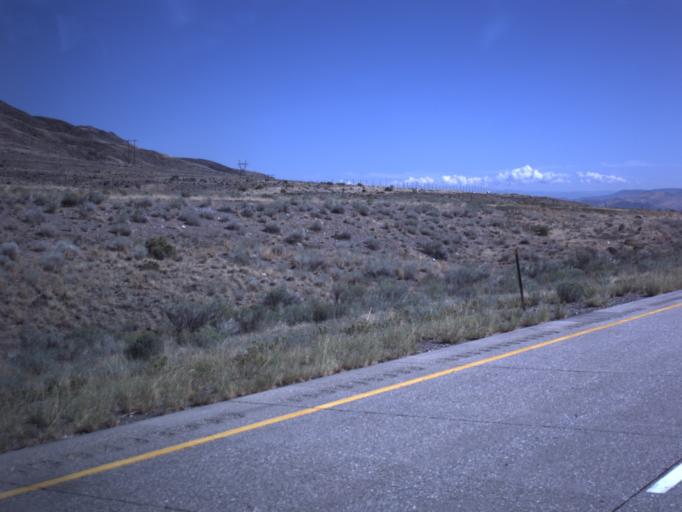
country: US
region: Utah
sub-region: Sevier County
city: Monroe
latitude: 38.6586
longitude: -112.1850
